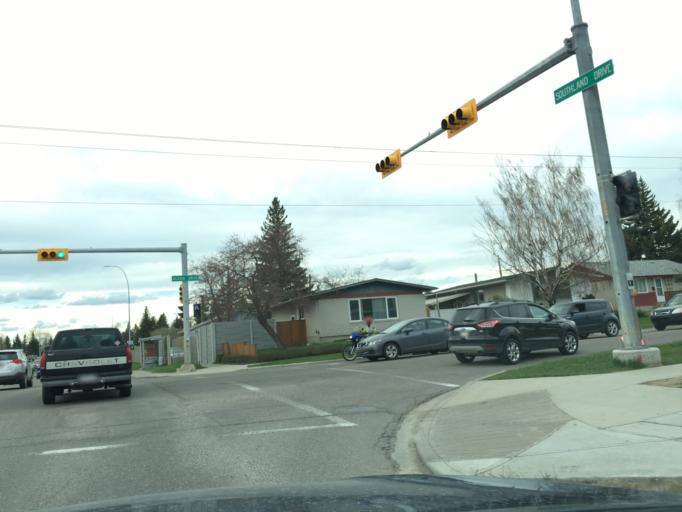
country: CA
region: Alberta
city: Calgary
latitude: 50.9641
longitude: -114.0482
